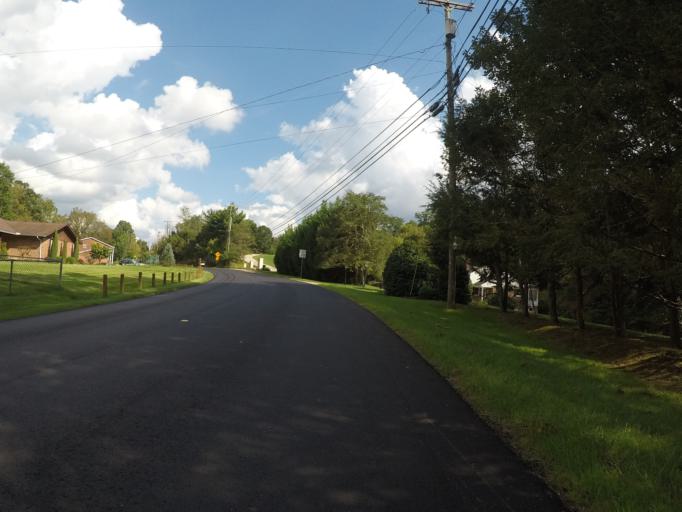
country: US
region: West Virginia
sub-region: Cabell County
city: Huntington
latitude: 38.3934
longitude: -82.4321
